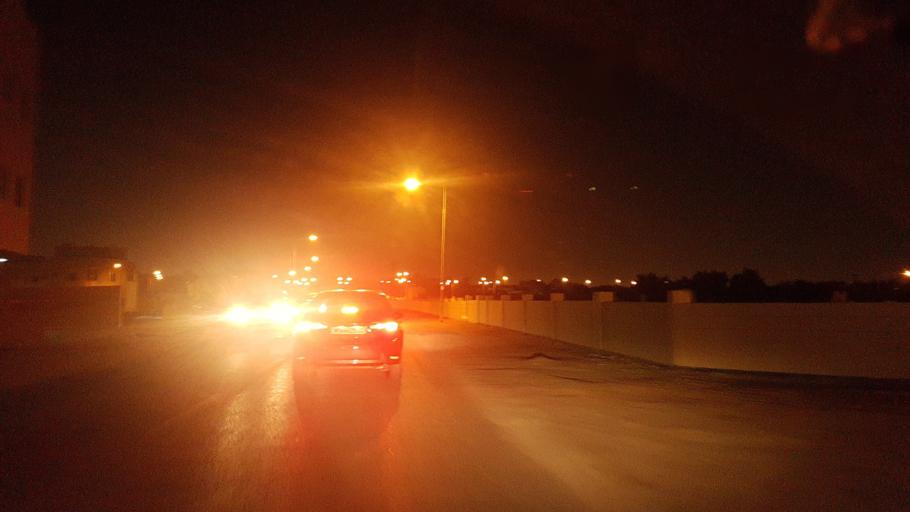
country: BH
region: Manama
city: Jidd Hafs
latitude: 26.2286
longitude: 50.5133
